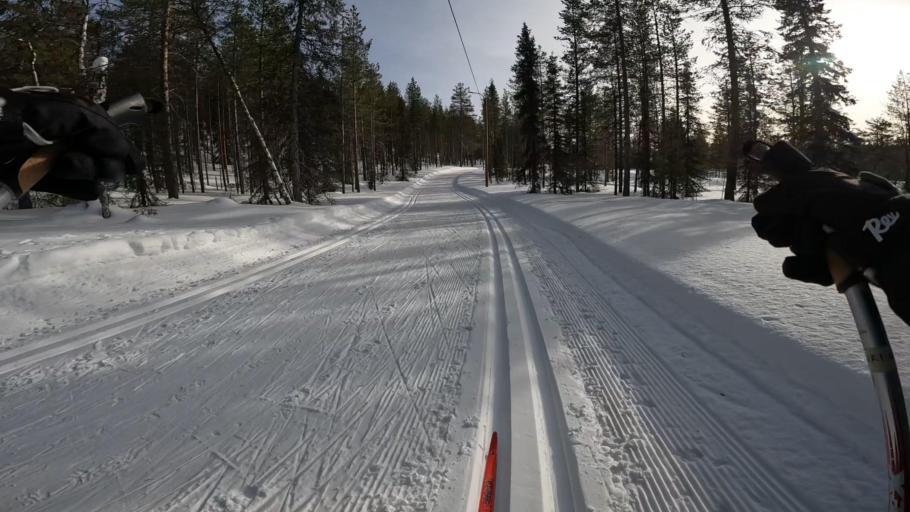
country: FI
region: Lapland
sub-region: Itae-Lappi
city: Salla
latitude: 66.7451
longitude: 28.8127
